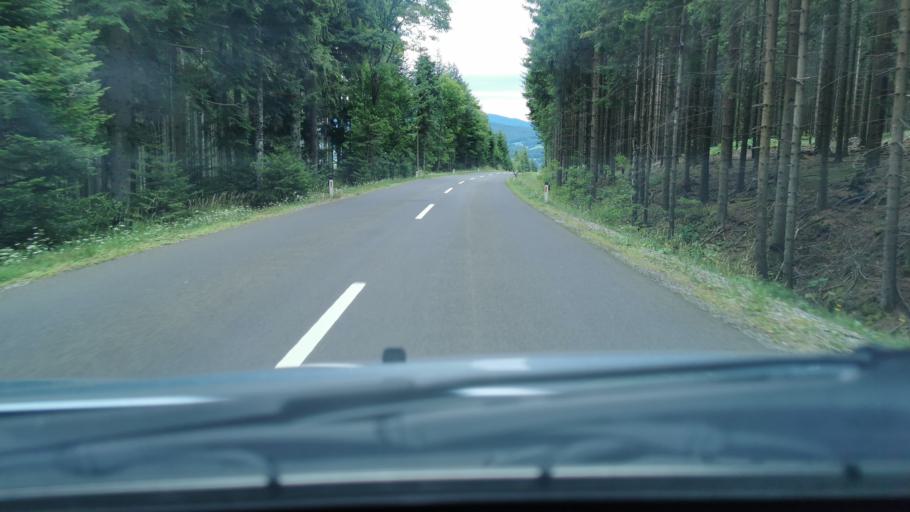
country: AT
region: Styria
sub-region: Politischer Bezirk Weiz
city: Fischbach
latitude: 47.4094
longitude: 15.6591
